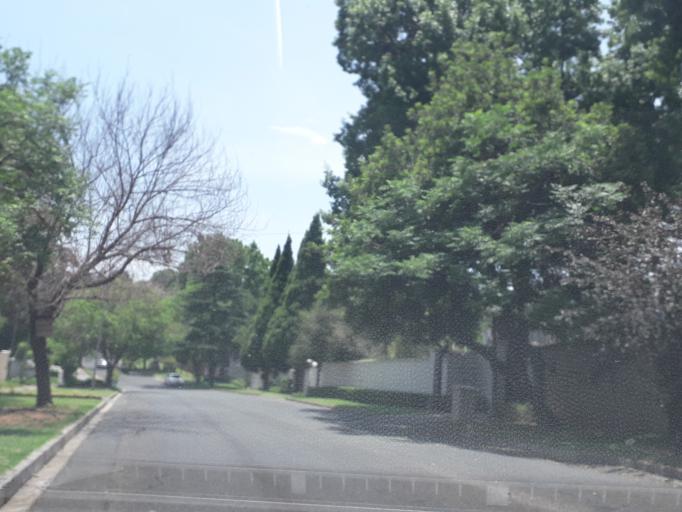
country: ZA
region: Gauteng
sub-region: City of Johannesburg Metropolitan Municipality
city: Johannesburg
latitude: -26.1342
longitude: 28.0298
